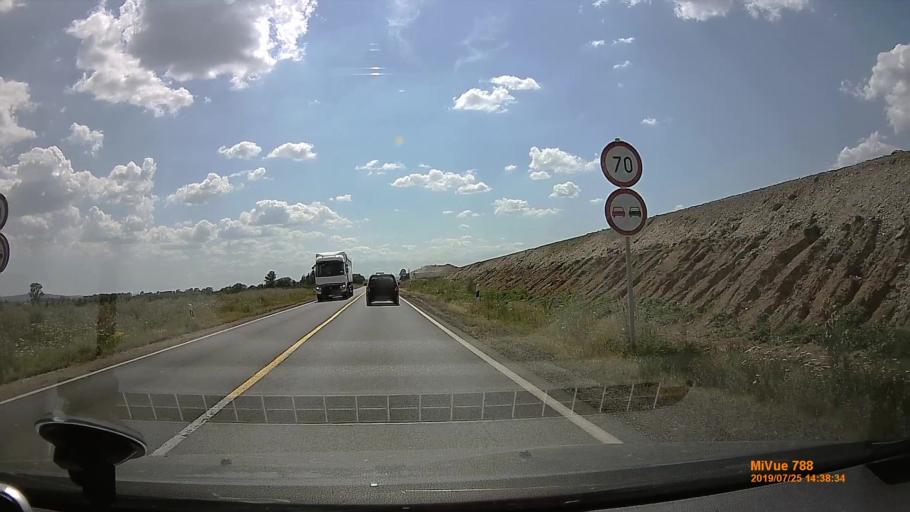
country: HU
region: Borsod-Abauj-Zemplen
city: Encs
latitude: 48.3051
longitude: 21.0635
